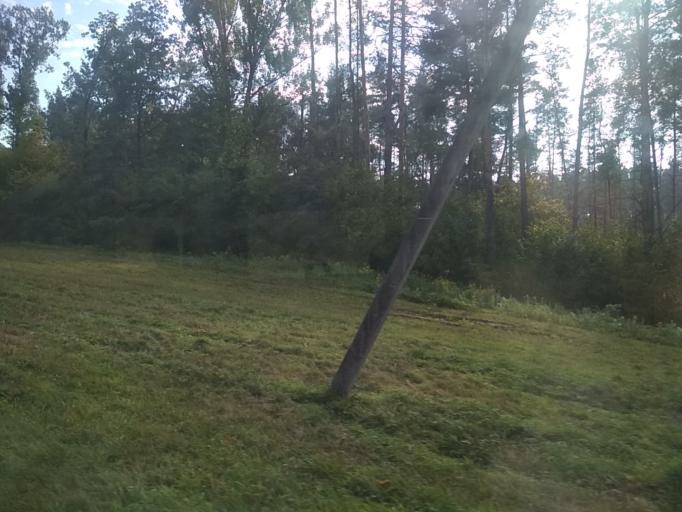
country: BY
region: Minsk
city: Machulishchy
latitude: 53.7841
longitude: 27.6077
